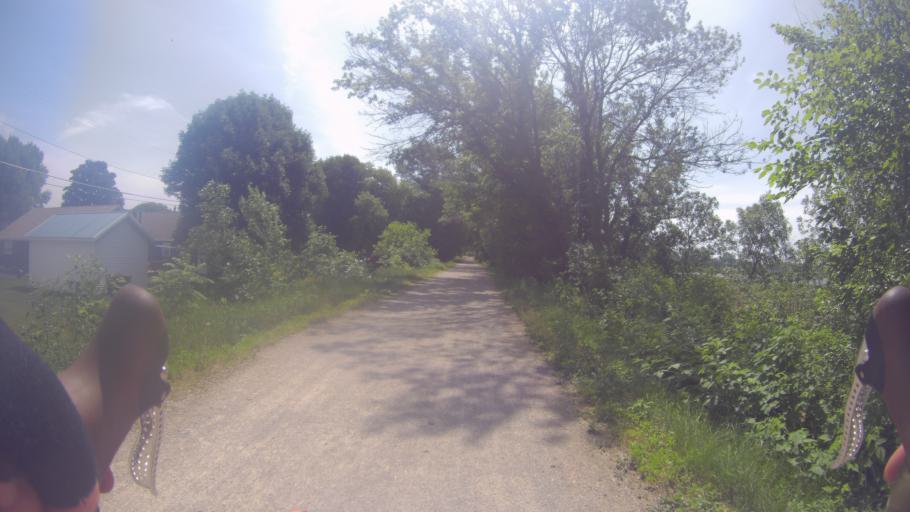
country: US
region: Wisconsin
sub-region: Jefferson County
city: Lake Mills
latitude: 43.0659
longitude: -88.9274
